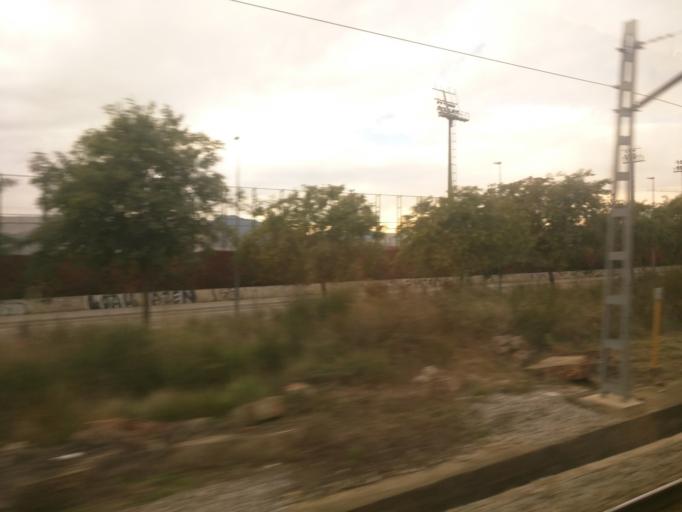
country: ES
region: Catalonia
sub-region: Provincia de Barcelona
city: Sant Feliu de Llobregat
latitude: 41.3764
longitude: 2.0541
